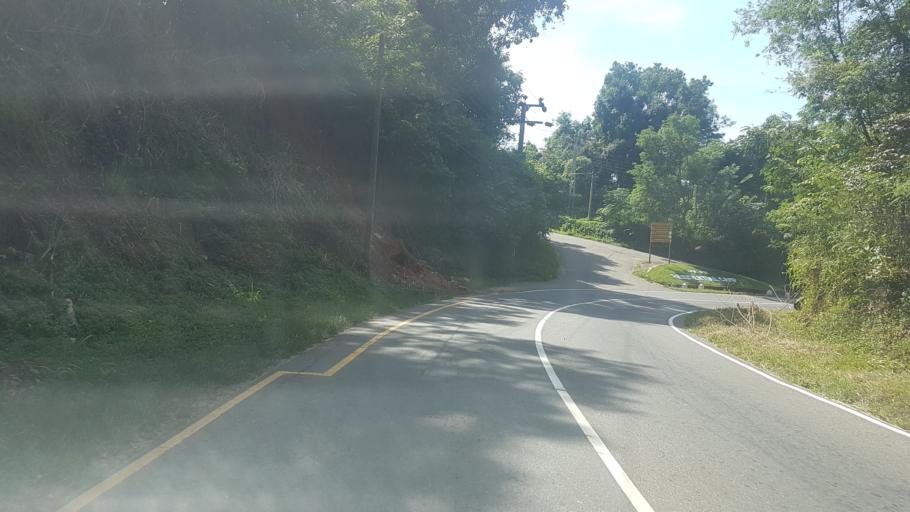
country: LK
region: Uva
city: Haputale
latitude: 6.8149
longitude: 81.0827
